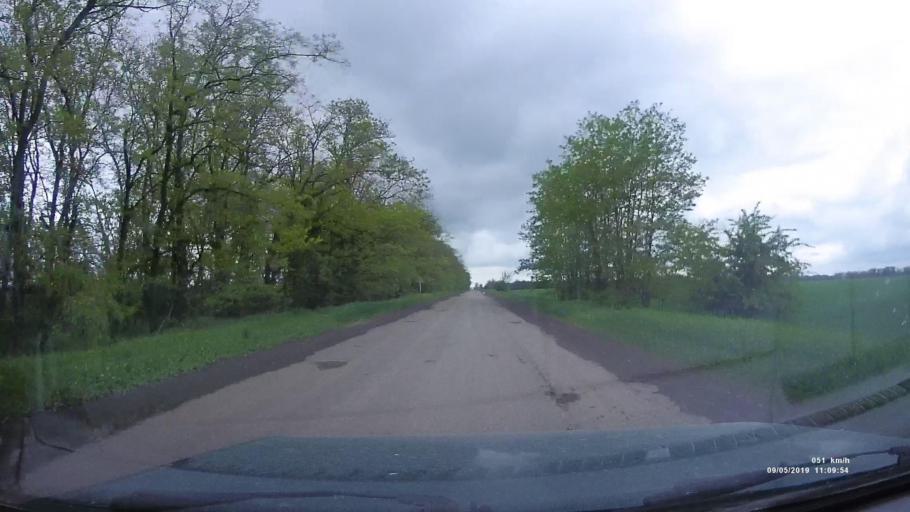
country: RU
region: Krasnodarskiy
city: Kanelovskaya
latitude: 46.7795
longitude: 39.2116
